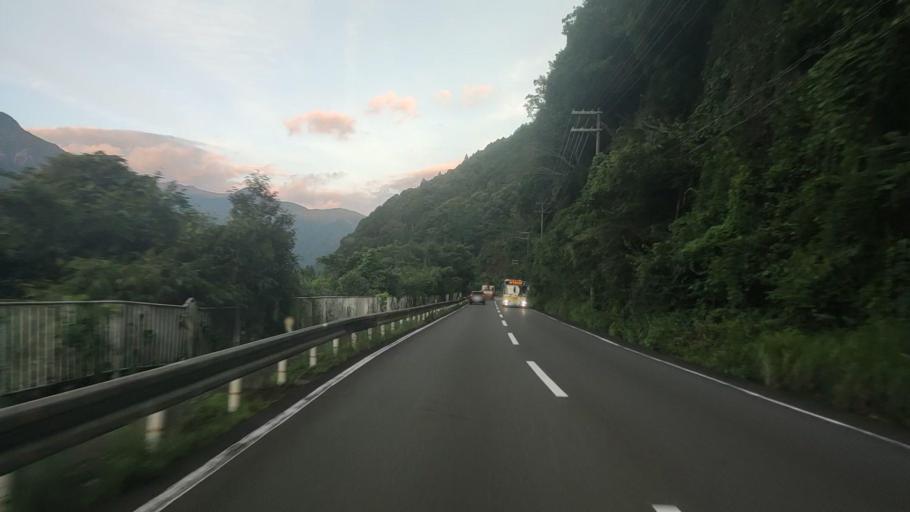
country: JP
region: Wakayama
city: Shingu
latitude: 33.8112
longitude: 135.8621
